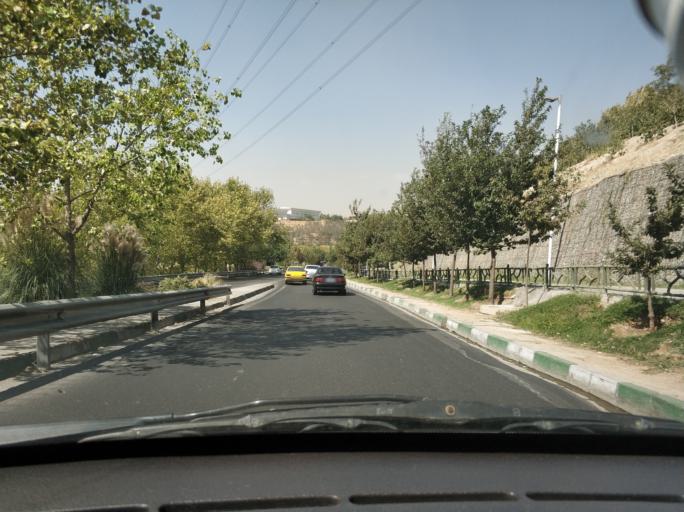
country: IR
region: Tehran
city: Tehran
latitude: 35.7416
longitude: 51.3717
